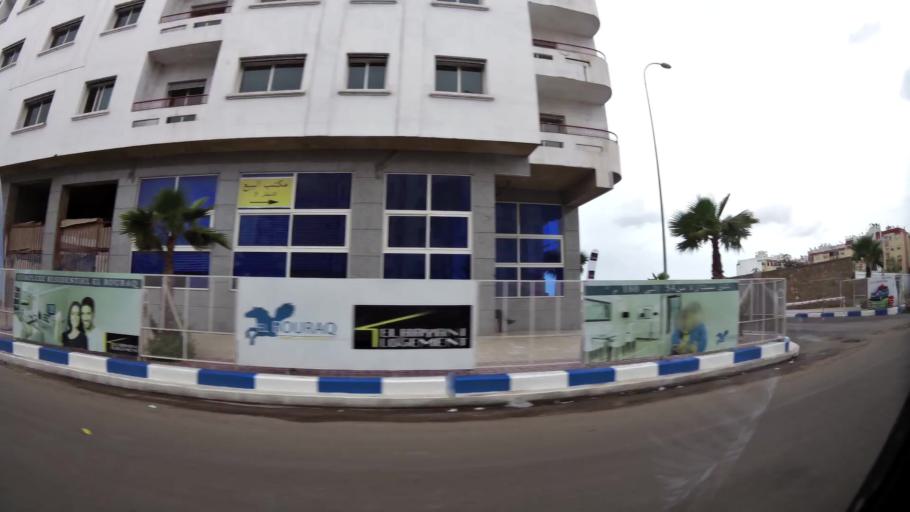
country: MA
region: Grand Casablanca
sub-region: Casablanca
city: Casablanca
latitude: 33.5754
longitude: -7.5557
